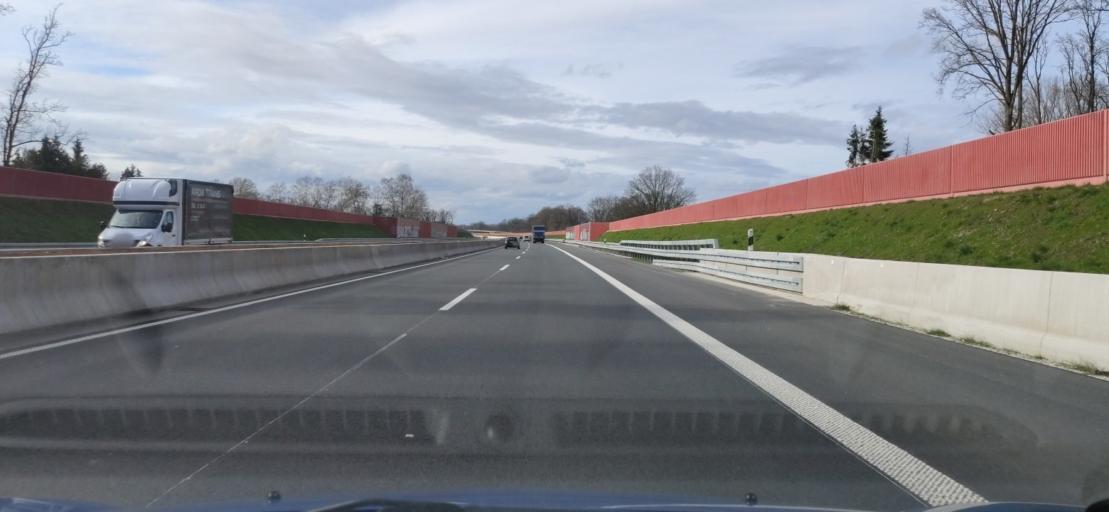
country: DE
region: North Rhine-Westphalia
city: Halle
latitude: 52.0612
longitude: 8.3270
